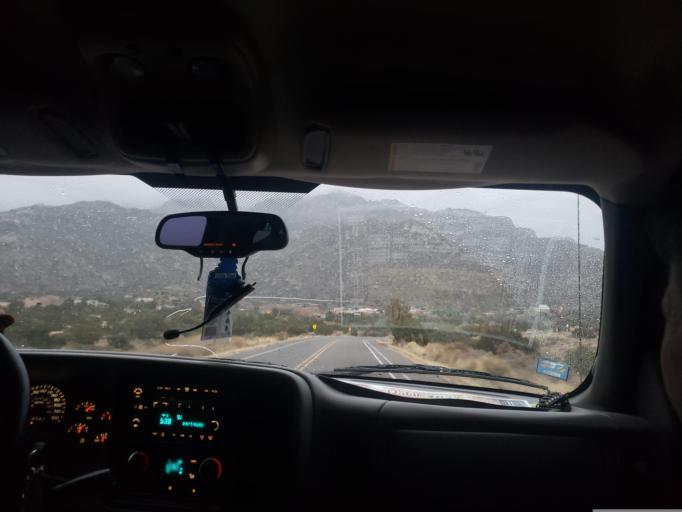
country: US
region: New Mexico
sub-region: Bernalillo County
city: Sandia Heights
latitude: 35.1908
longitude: -106.4892
